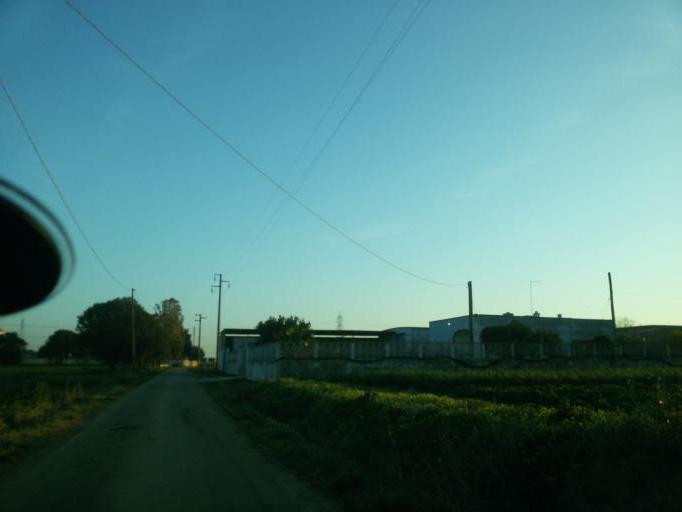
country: IT
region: Apulia
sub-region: Provincia di Brindisi
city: La Rosa
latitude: 40.6038
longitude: 17.9394
